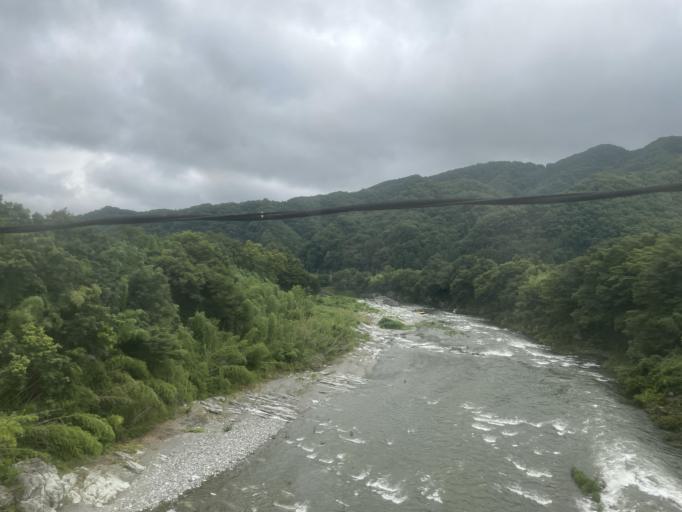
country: JP
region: Saitama
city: Yorii
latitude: 36.0840
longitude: 139.1144
